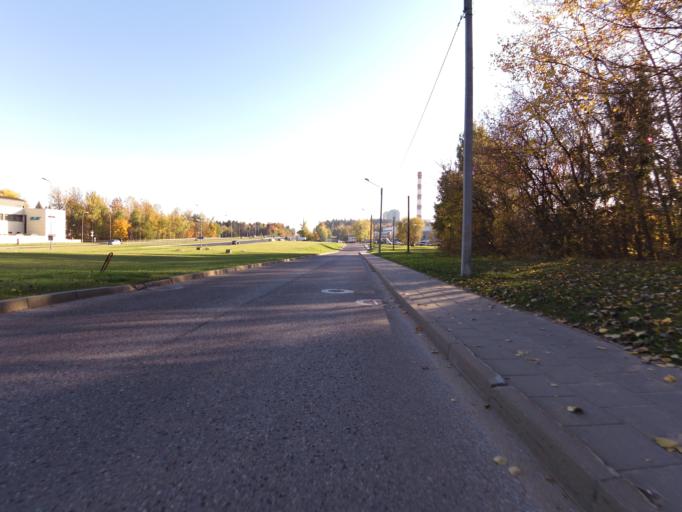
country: LT
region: Vilnius County
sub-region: Vilnius
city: Fabijoniskes
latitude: 54.7393
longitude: 25.2631
